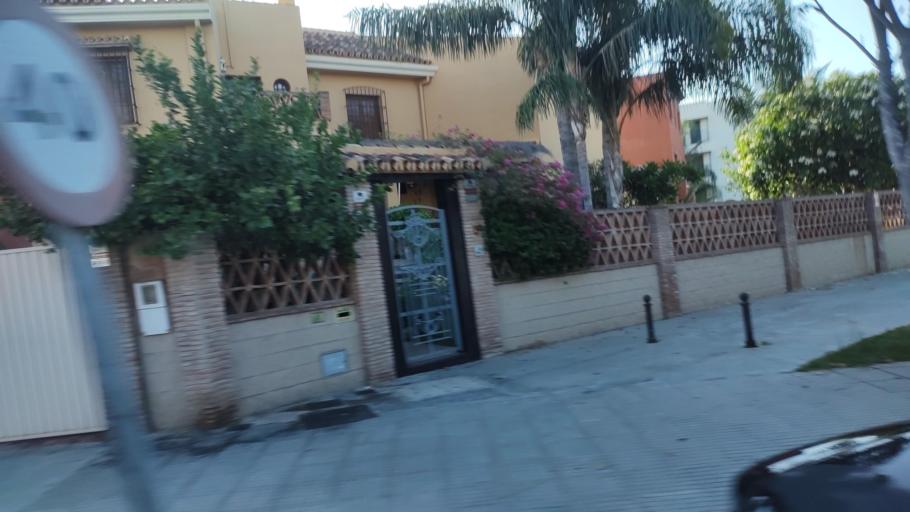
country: ES
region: Andalusia
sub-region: Provincia de Malaga
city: Torremolinos
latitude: 36.6385
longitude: -4.4886
